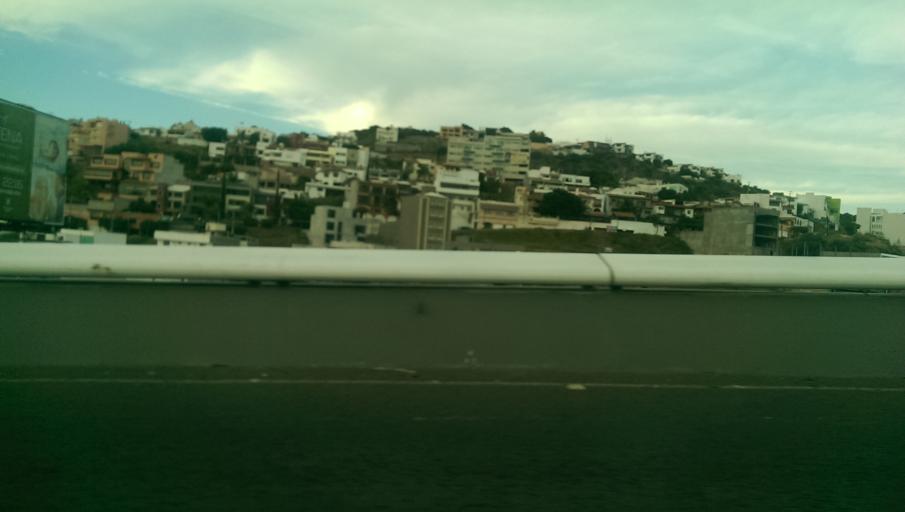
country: MX
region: Queretaro
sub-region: Queretaro
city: Santiago de Queretaro
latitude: 20.5895
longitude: -100.3647
